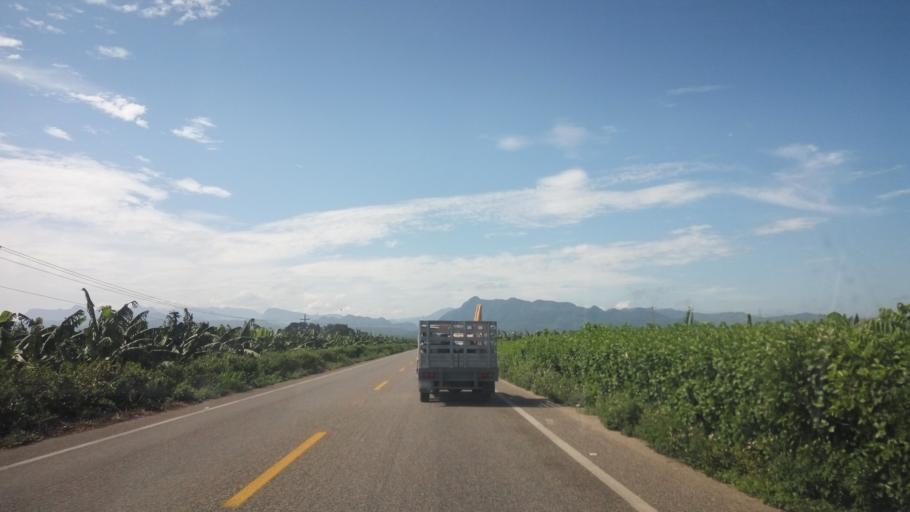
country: MX
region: Tabasco
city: Teapa
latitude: 17.6109
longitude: -92.9653
